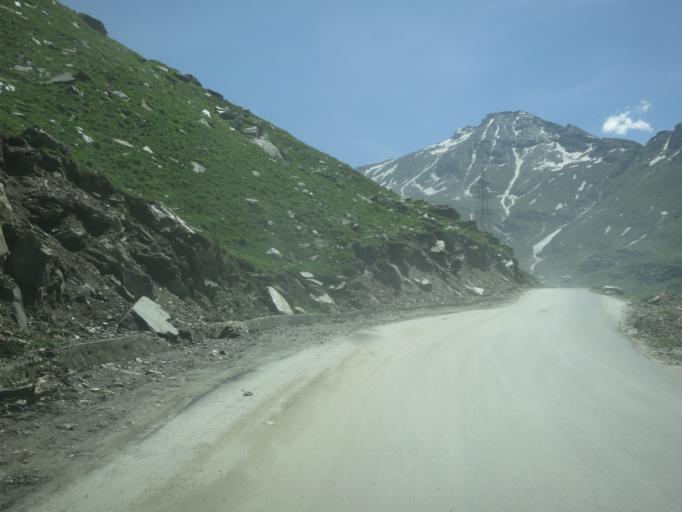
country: IN
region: Himachal Pradesh
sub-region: Kulu
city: Manali
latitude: 32.3546
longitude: 77.2203
